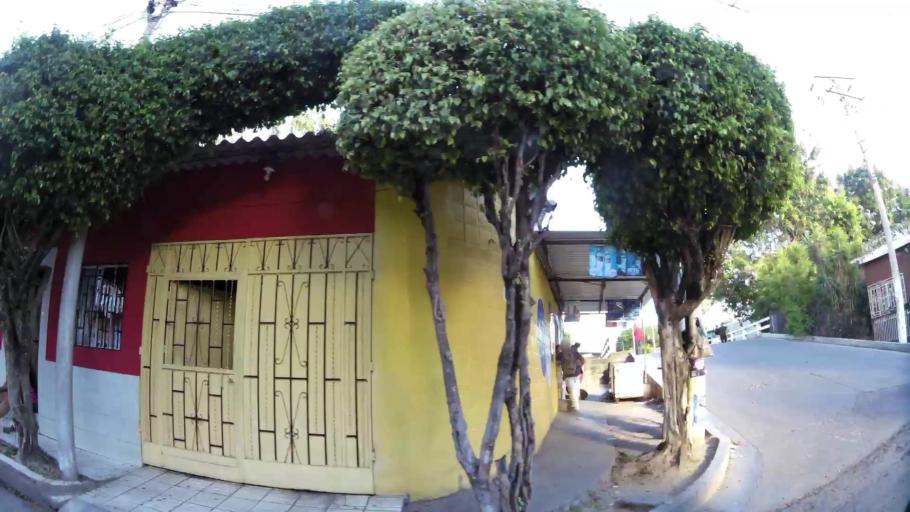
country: SV
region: Santa Ana
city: Metapan
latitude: 14.3326
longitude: -89.4519
